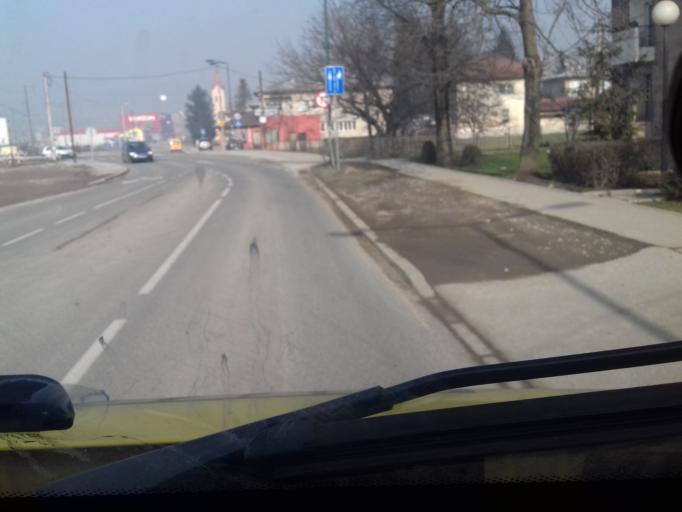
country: BA
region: Federation of Bosnia and Herzegovina
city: Ilijas
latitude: 43.9609
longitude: 18.2647
